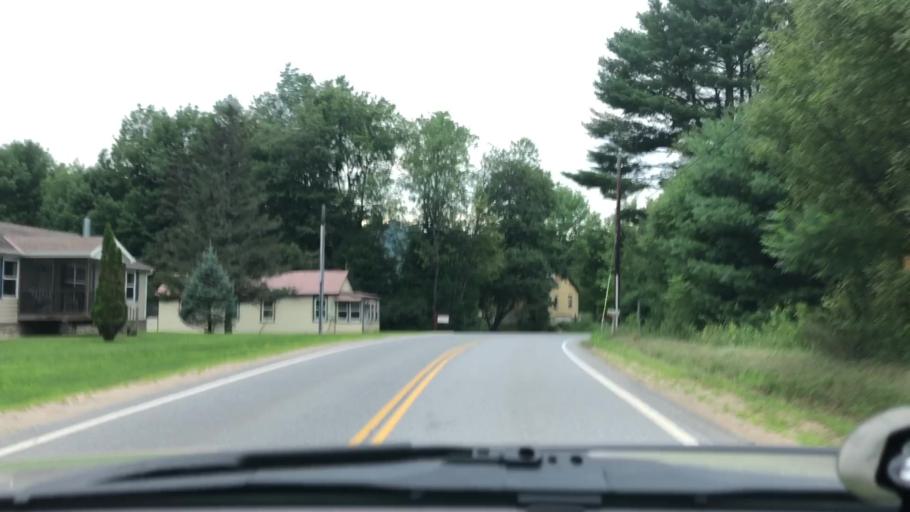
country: US
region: New York
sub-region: Saratoga County
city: Corinth
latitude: 43.2196
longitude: -73.8107
